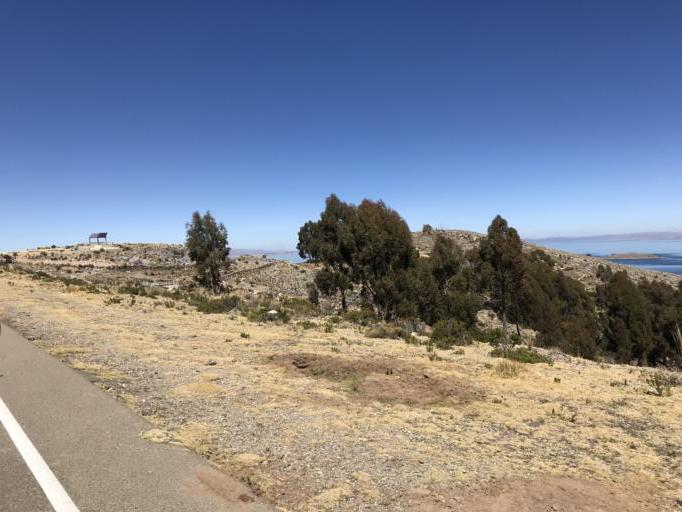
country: BO
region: La Paz
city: San Pedro
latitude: -16.1997
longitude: -68.9089
